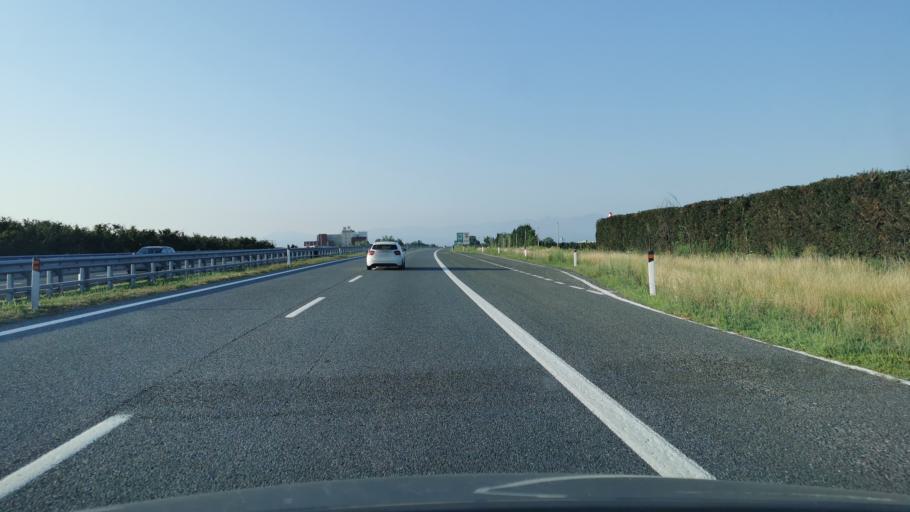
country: IT
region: Piedmont
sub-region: Provincia di Cuneo
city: Salmour
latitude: 44.5600
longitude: 7.7835
